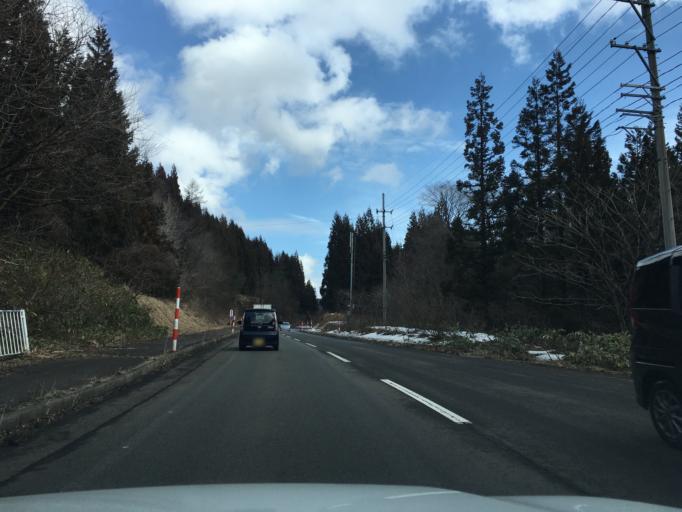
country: JP
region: Akita
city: Takanosu
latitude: 40.0862
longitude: 140.3271
